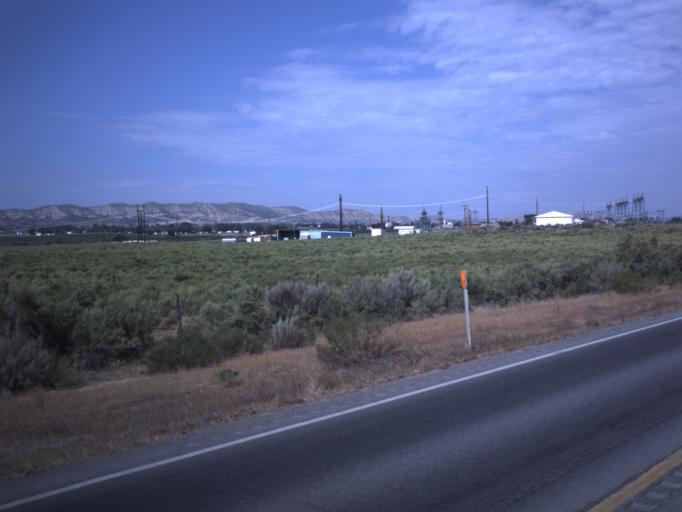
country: US
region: Utah
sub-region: Uintah County
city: Naples
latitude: 40.3970
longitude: -109.4588
